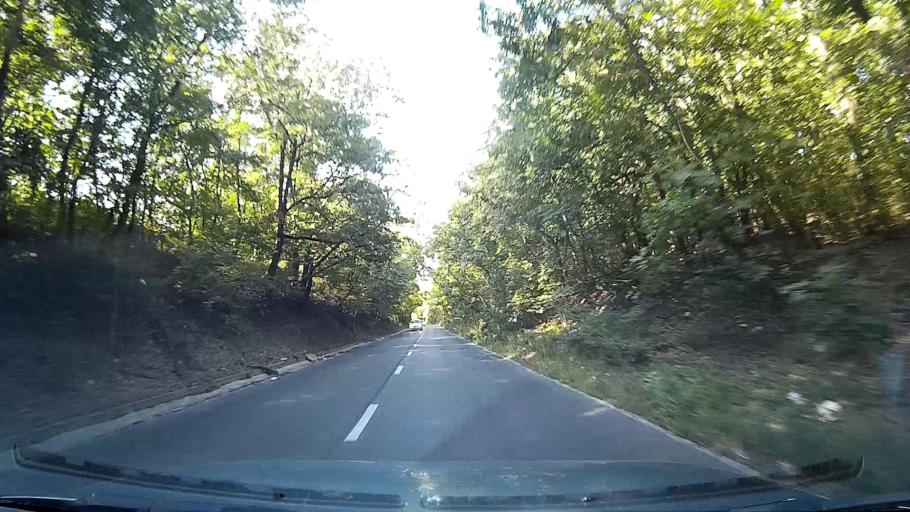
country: HU
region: Pest
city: Diosd
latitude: 47.4290
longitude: 18.9805
